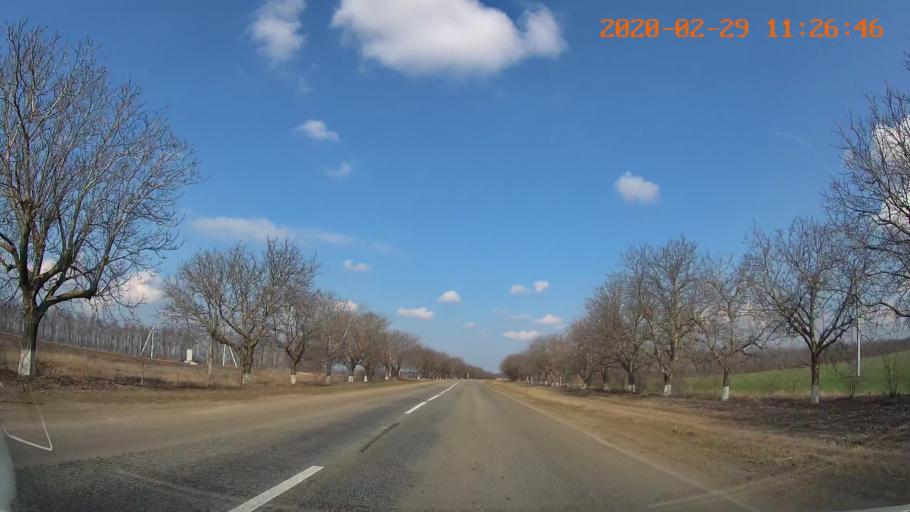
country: MD
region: Telenesti
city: Cocieri
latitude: 47.4579
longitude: 29.1447
